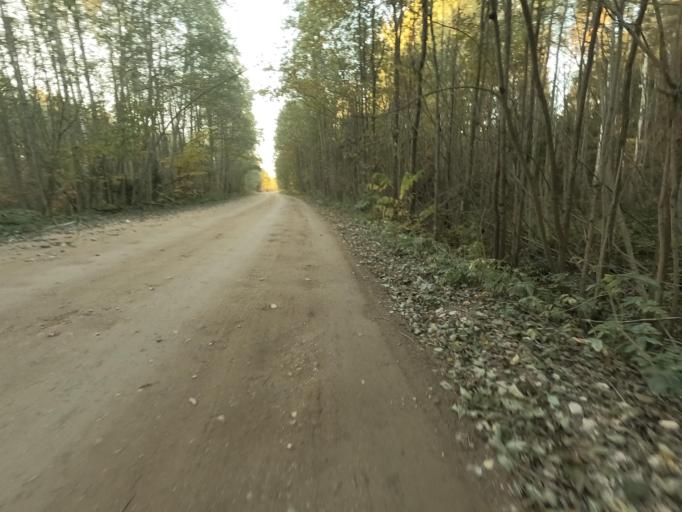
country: RU
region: Leningrad
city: Lyuban'
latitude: 58.9976
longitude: 31.1044
